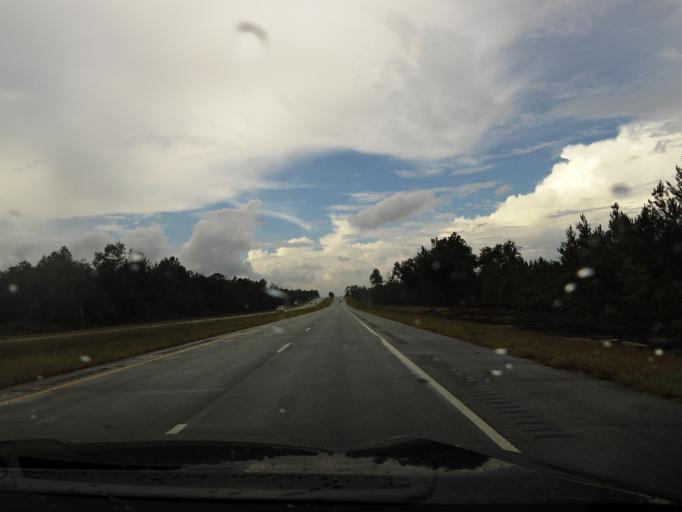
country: US
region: Georgia
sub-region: Wayne County
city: Jesup
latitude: 31.6146
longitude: -81.8615
